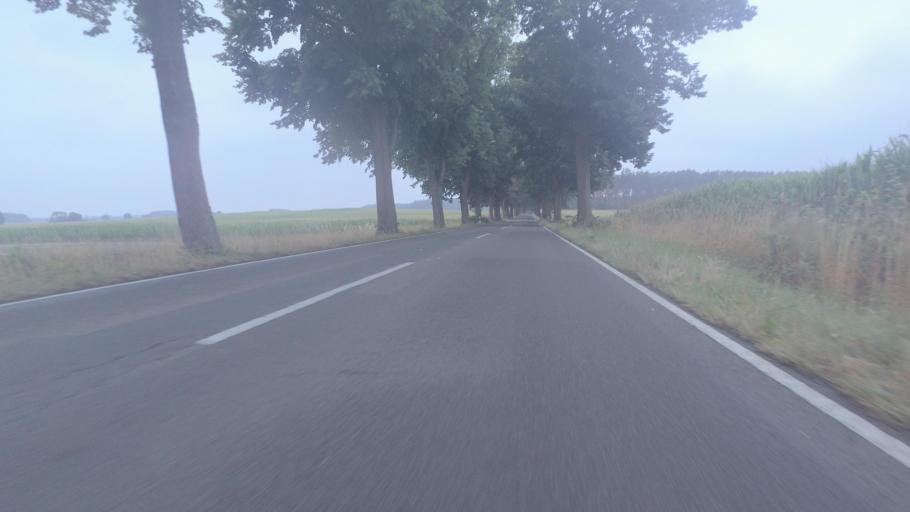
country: DE
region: Brandenburg
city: Heiligengrabe
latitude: 53.1117
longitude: 12.3722
